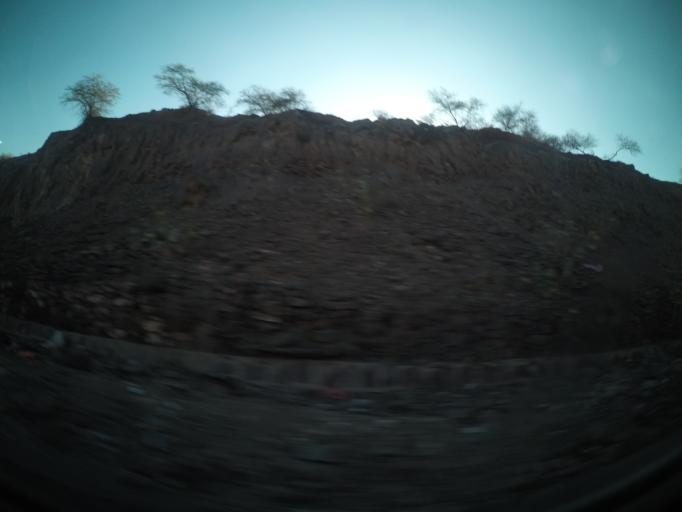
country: YE
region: Ad Dali'
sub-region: Ad Dhale'e
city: Dhalie
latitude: 13.6724
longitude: 44.7660
